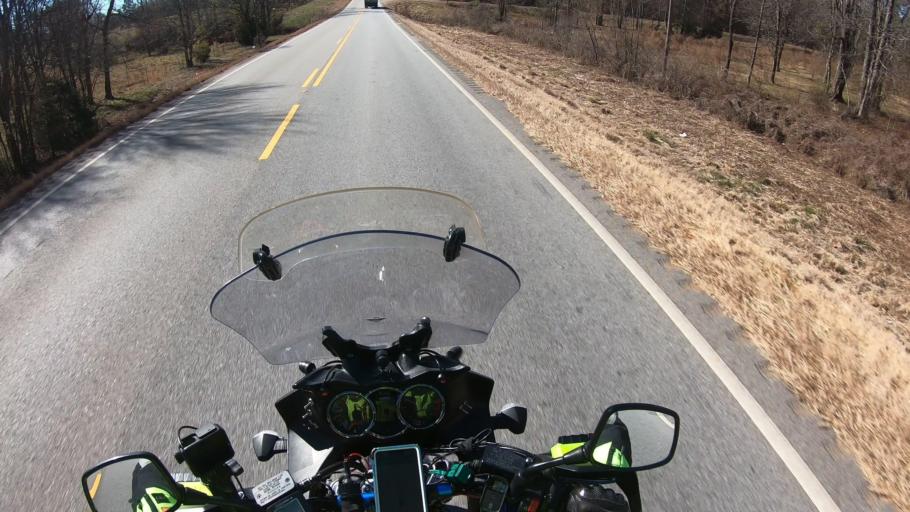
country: US
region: Alabama
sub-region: Calhoun County
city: Choccolocco
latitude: 33.4914
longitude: -85.6754
